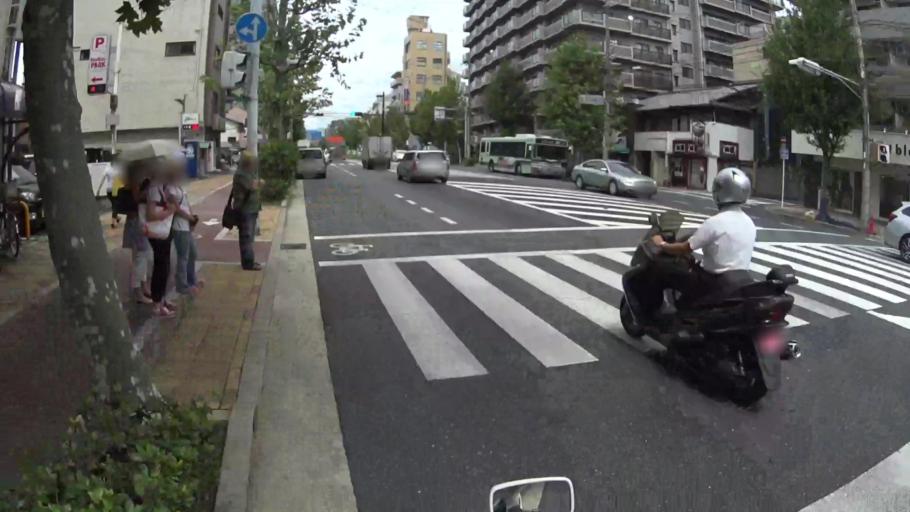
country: JP
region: Kyoto
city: Kyoto
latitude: 35.0058
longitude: 135.7318
